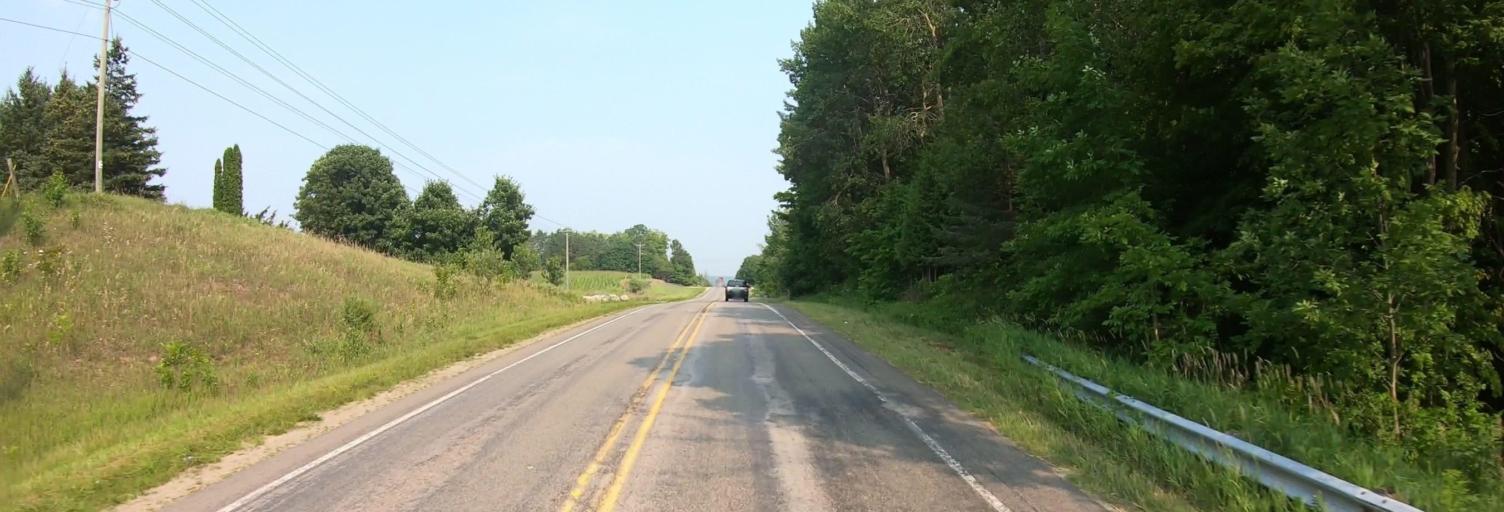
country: US
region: Michigan
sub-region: Charlevoix County
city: Charlevoix
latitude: 45.1845
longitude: -85.2793
